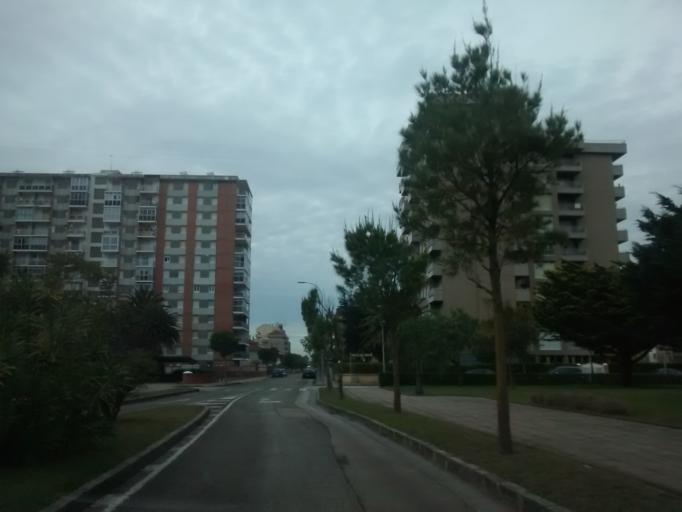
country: ES
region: Cantabria
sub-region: Provincia de Cantabria
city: Santona
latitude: 43.4248
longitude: -3.4468
